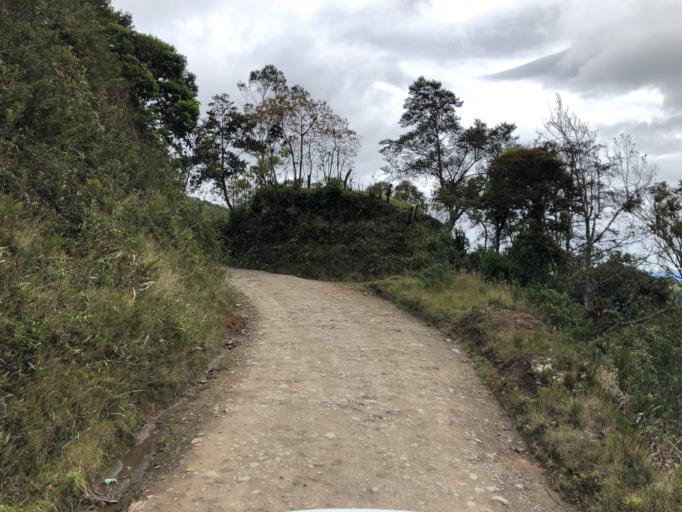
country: CO
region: Cauca
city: Totoro
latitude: 2.5080
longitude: -76.3612
